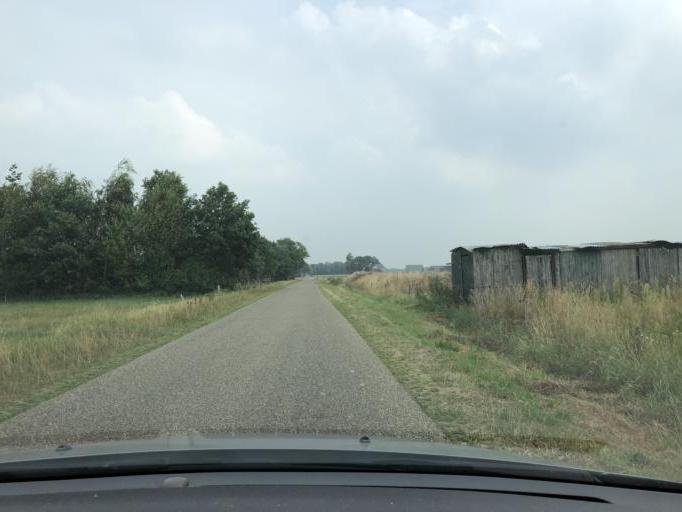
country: NL
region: Overijssel
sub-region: Gemeente Dalfsen
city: Dalfsen
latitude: 52.6012
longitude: 6.3410
